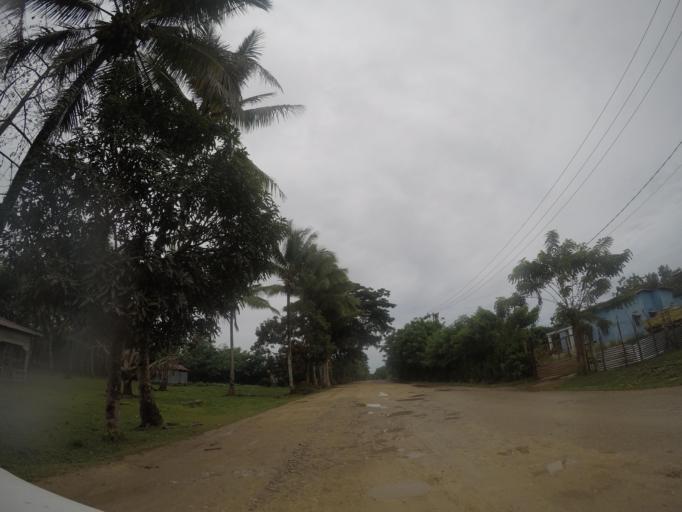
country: TL
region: Lautem
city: Lospalos
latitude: -8.5077
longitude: 126.9914
